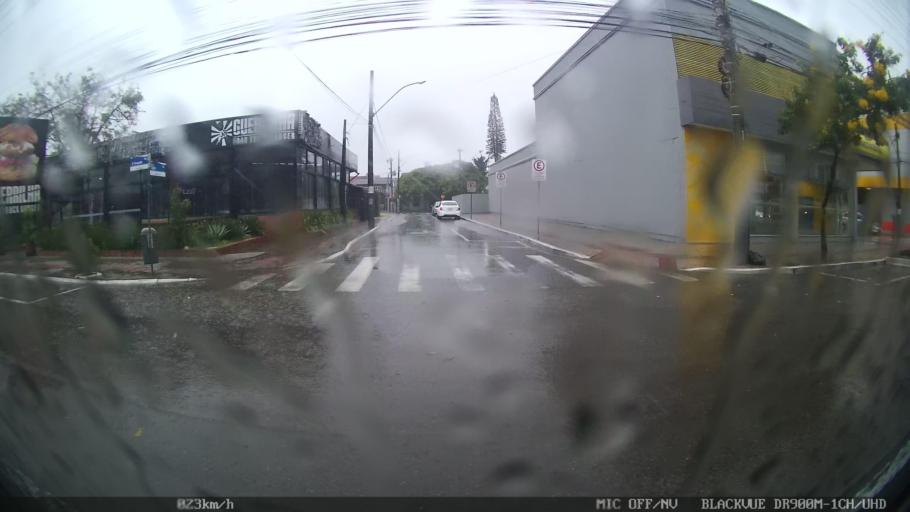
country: BR
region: Santa Catarina
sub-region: Balneario Camboriu
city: Balneario Camboriu
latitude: -26.9980
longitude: -48.6385
